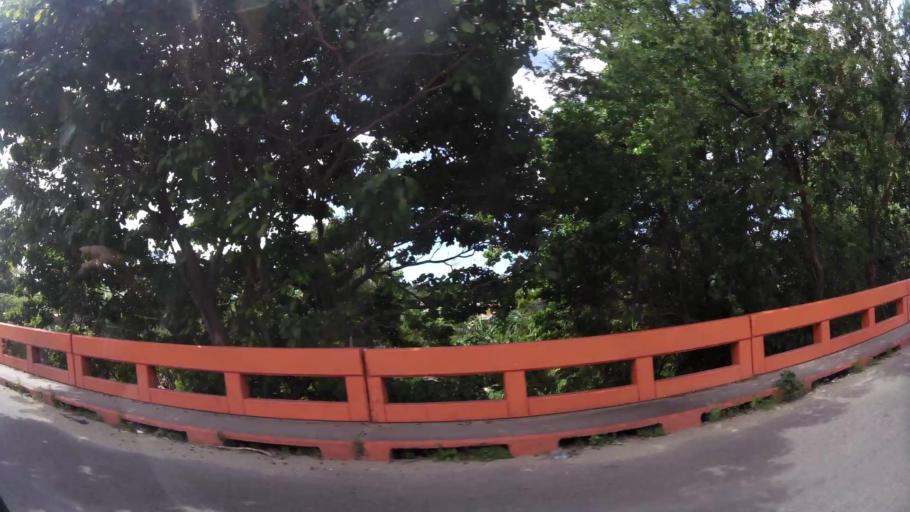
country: DO
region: San Cristobal
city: San Cristobal
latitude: 18.4256
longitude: -70.1171
